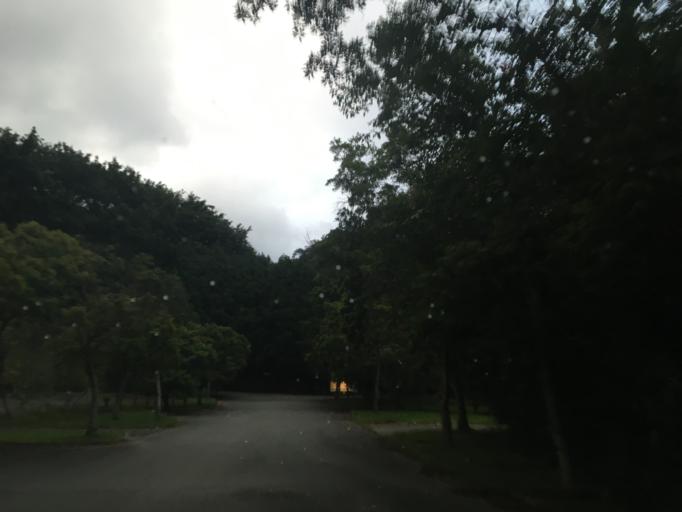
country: TW
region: Taiwan
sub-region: Nantou
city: Puli
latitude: 23.9025
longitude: 120.9118
